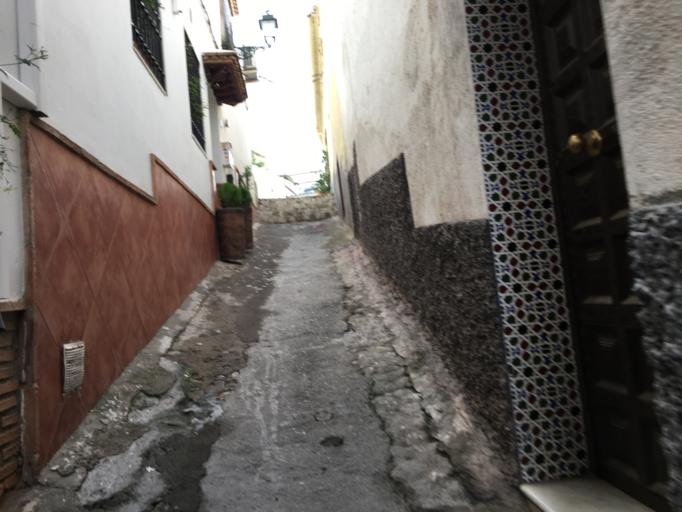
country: ES
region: Andalusia
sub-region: Provincia de Granada
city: Granada
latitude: 37.1827
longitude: -3.5953
